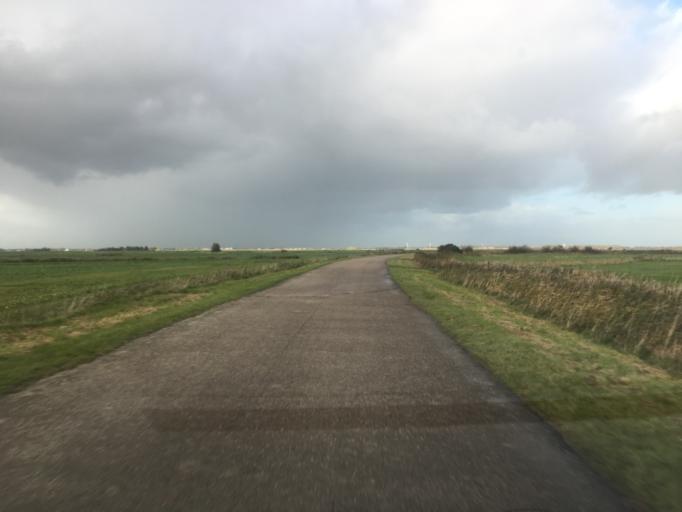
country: DE
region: Schleswig-Holstein
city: Neukirchen
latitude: 54.9145
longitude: 8.7508
